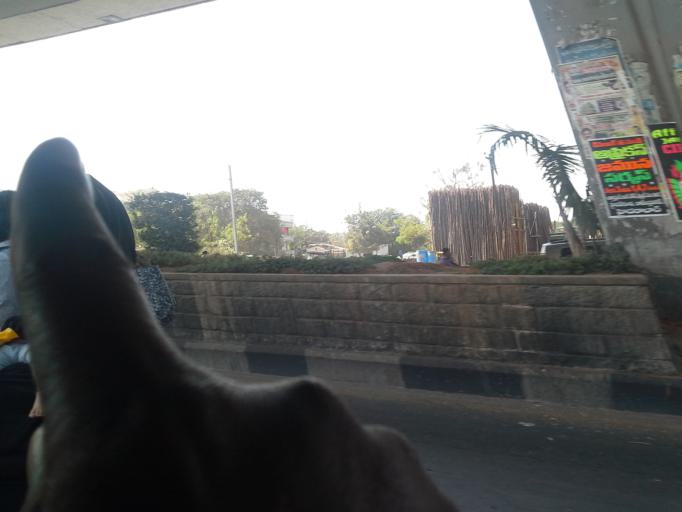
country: IN
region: Telangana
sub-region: Hyderabad
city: Hyderabad
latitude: 17.3625
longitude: 78.4280
